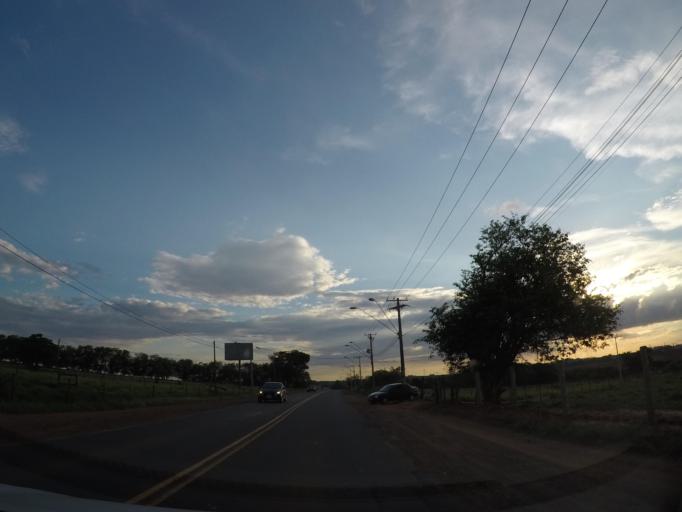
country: BR
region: Sao Paulo
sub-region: Sumare
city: Sumare
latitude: -22.8443
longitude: -47.2795
